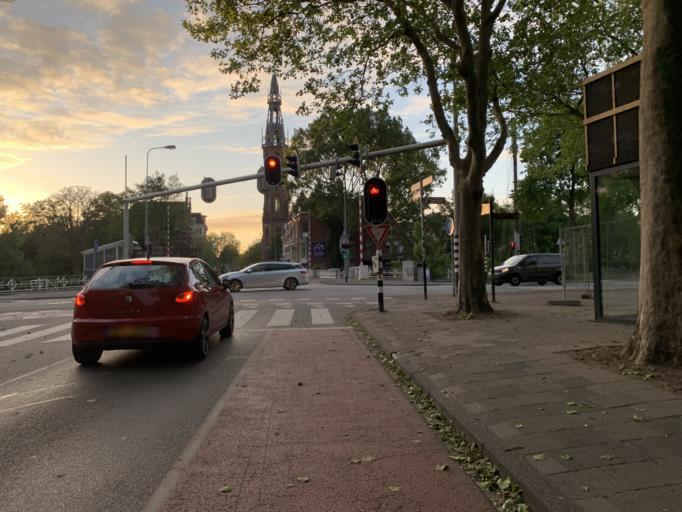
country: NL
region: Groningen
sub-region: Gemeente Groningen
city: Groningen
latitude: 53.2133
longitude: 6.5741
